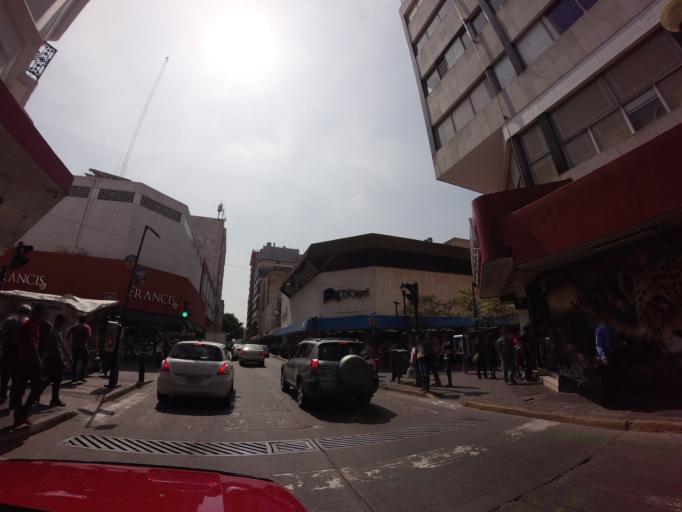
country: MX
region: Jalisco
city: Guadalajara
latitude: 20.6744
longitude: -103.3482
